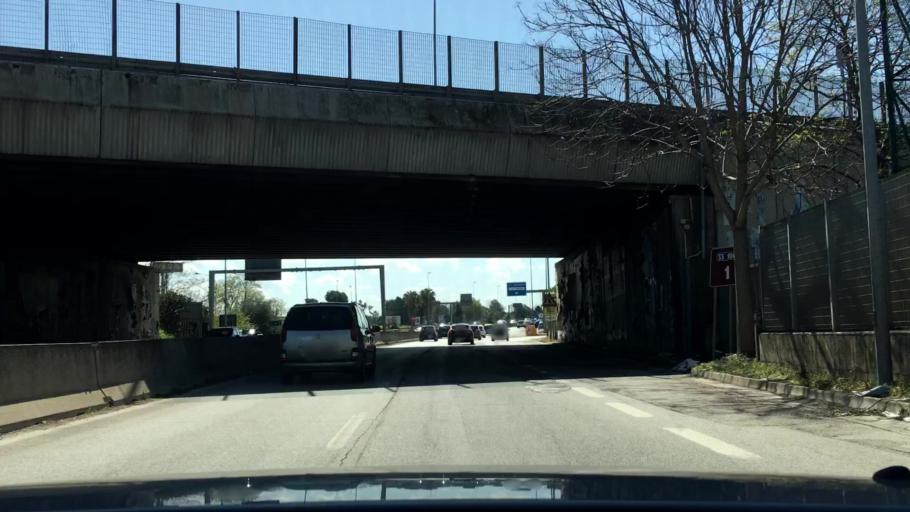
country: IT
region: Apulia
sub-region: Provincia di Bari
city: Triggiano
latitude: 41.0910
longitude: 16.8931
